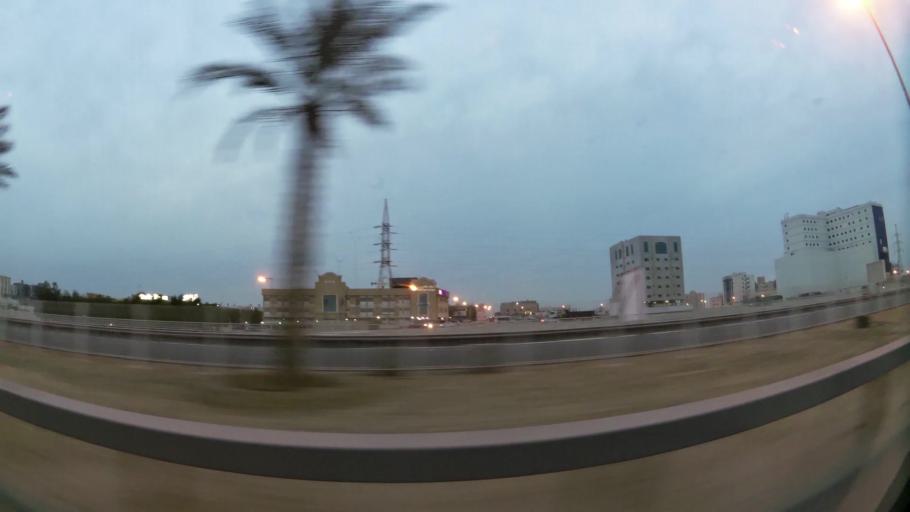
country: BH
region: Northern
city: Ar Rifa'
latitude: 26.1535
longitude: 50.5714
